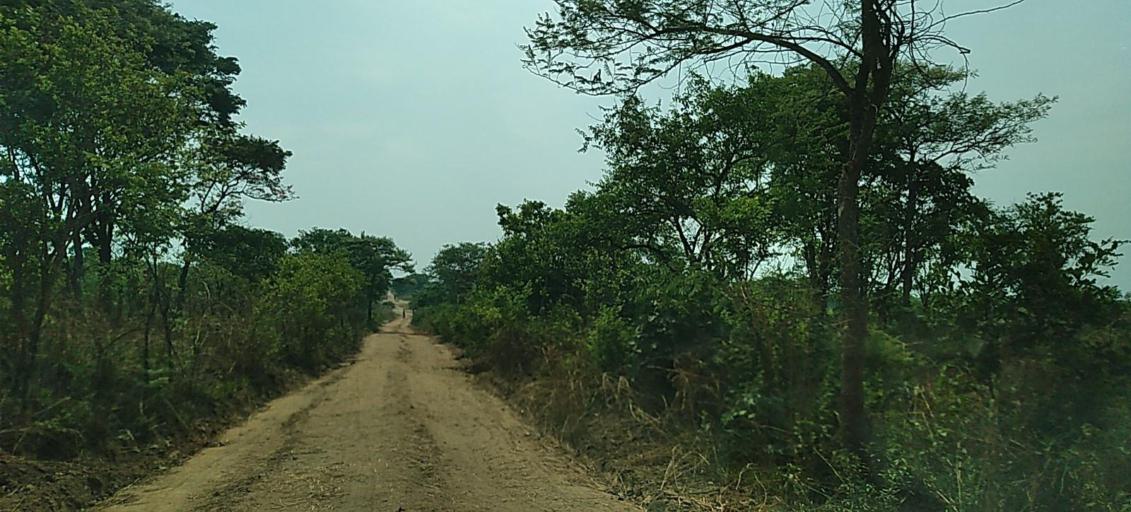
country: ZM
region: Copperbelt
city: Ndola
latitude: -13.2096
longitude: 28.7356
